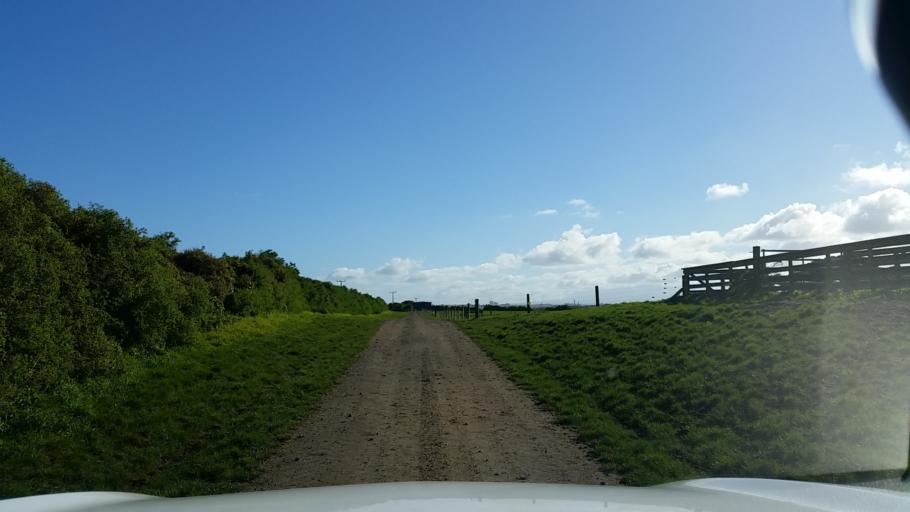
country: NZ
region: Taranaki
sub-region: South Taranaki District
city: Hawera
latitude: -39.6613
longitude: 174.3642
